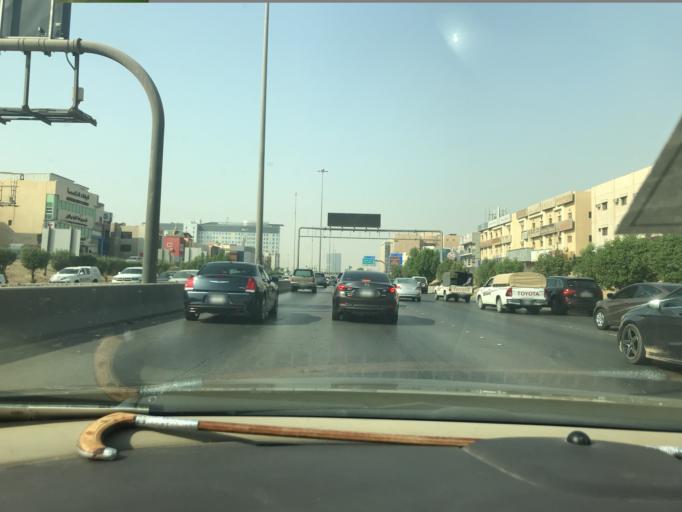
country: SA
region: Ar Riyad
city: Riyadh
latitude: 24.6823
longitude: 46.6967
